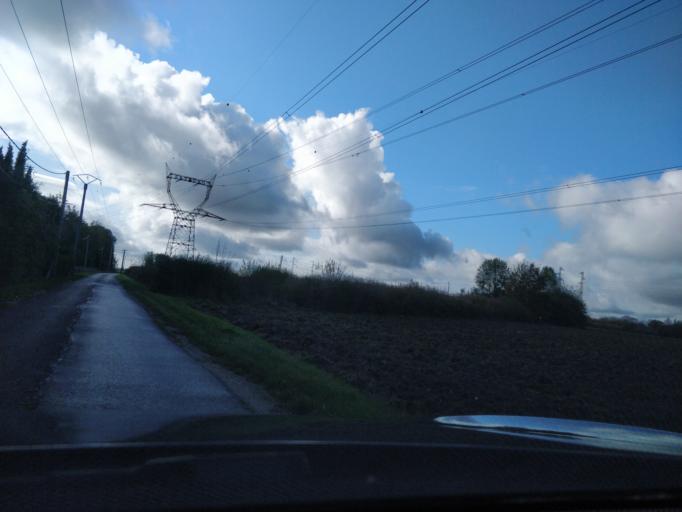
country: FR
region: Ile-de-France
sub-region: Departement de l'Essonne
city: Fontenay-les-Briis
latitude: 48.6330
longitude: 2.1529
